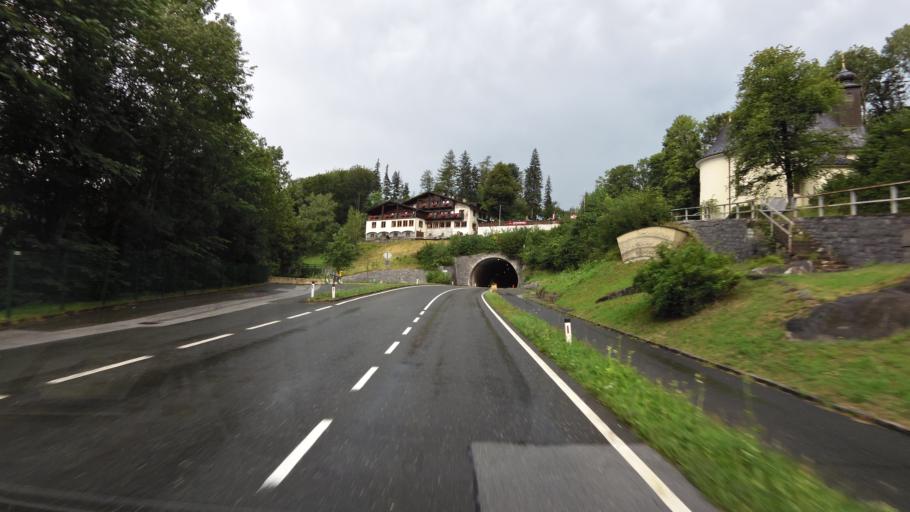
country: AT
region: Salzburg
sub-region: Politischer Bezirk Hallein
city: Scheffau am Tennengebirge
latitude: 47.5748
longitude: 13.1949
